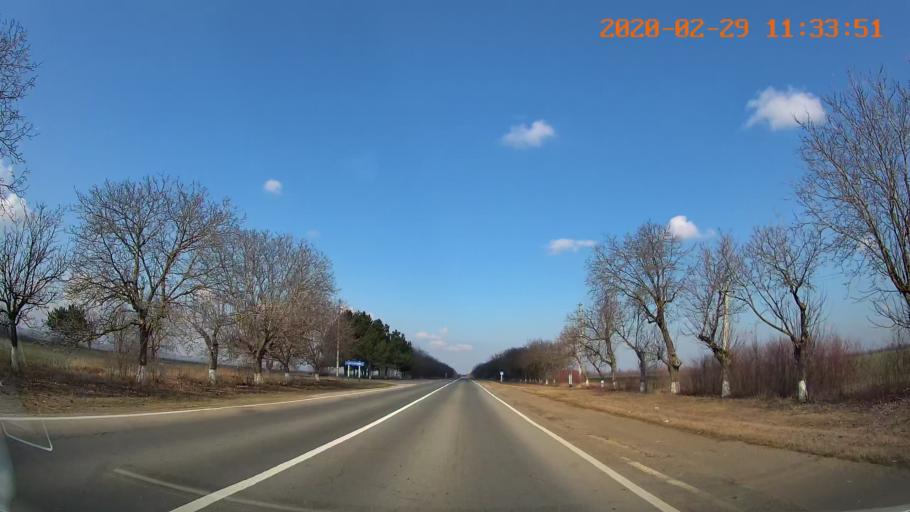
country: MD
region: Rezina
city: Saharna
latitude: 47.5572
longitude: 29.0802
